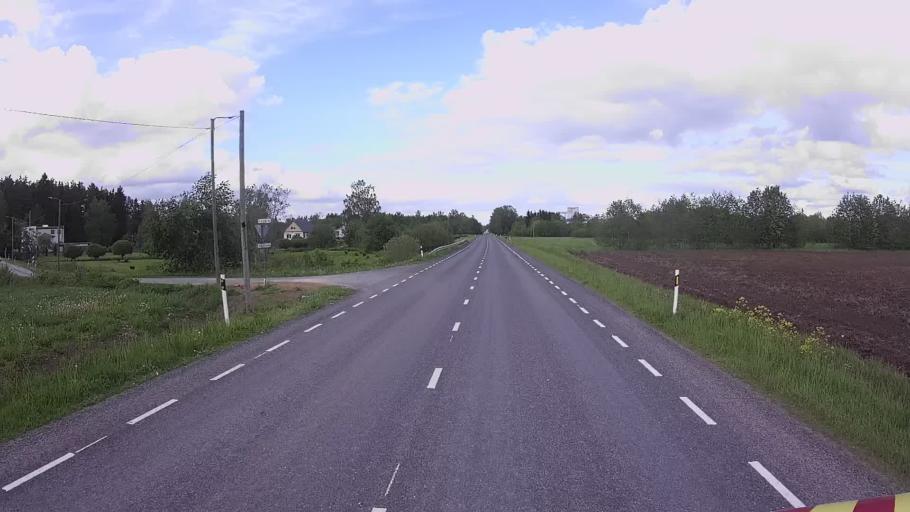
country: EE
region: Jogevamaa
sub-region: Mustvee linn
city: Mustvee
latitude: 58.9917
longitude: 26.8839
